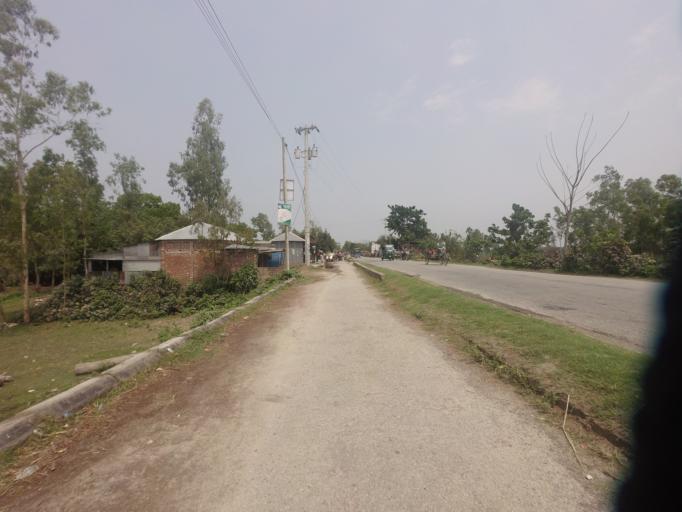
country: BD
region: Rajshahi
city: Sirajganj
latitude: 24.3600
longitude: 89.7060
